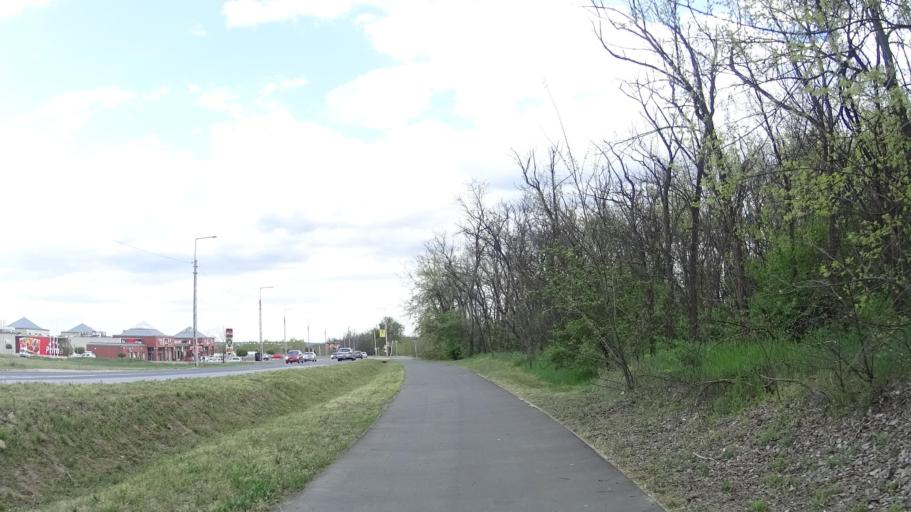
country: HU
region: Pest
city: Szada
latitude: 47.6245
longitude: 19.3234
